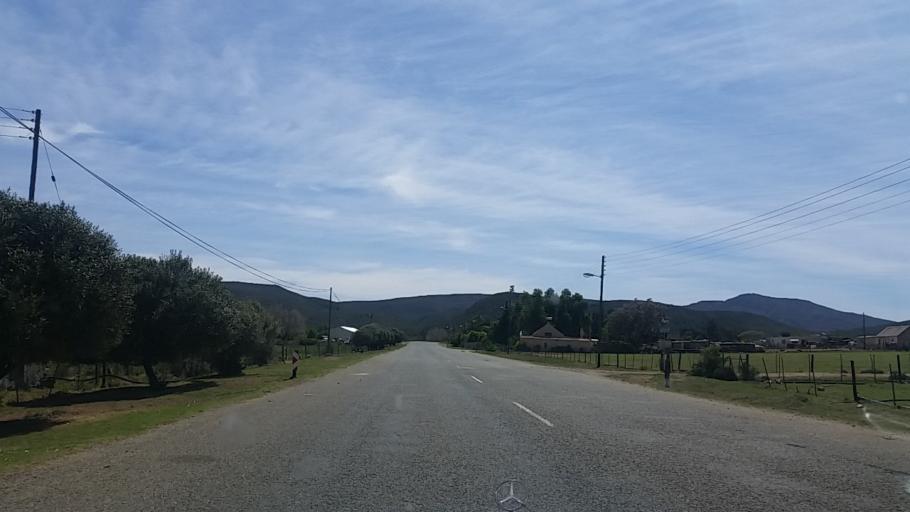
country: ZA
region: Western Cape
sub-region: Eden District Municipality
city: Knysna
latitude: -33.6476
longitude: 23.1357
